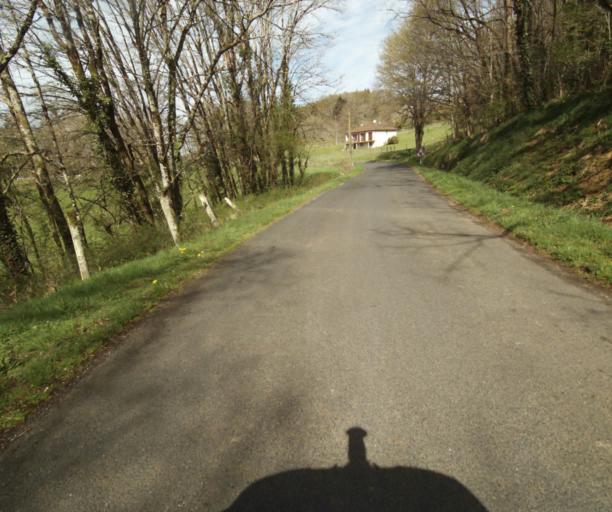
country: FR
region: Limousin
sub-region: Departement de la Correze
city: Laguenne
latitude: 45.2465
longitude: 1.8029
